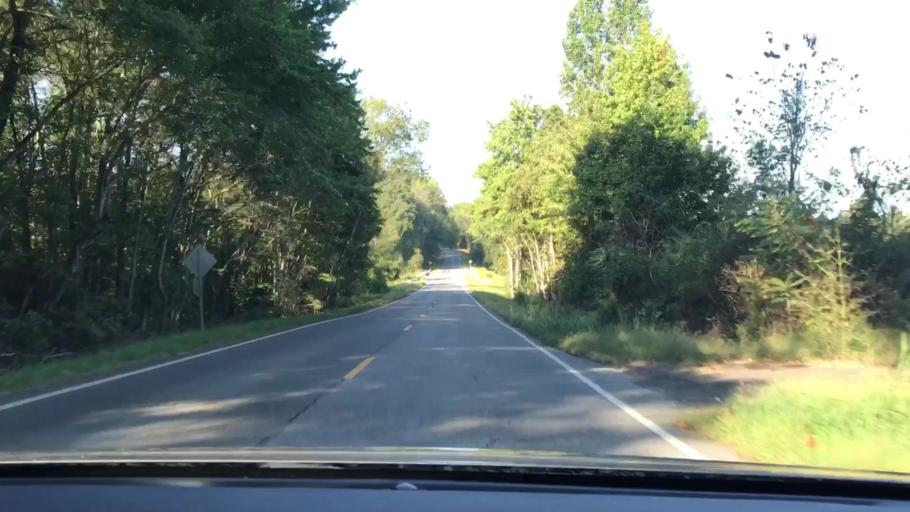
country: US
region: Kentucky
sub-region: Marshall County
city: Benton
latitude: 36.7668
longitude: -88.1856
